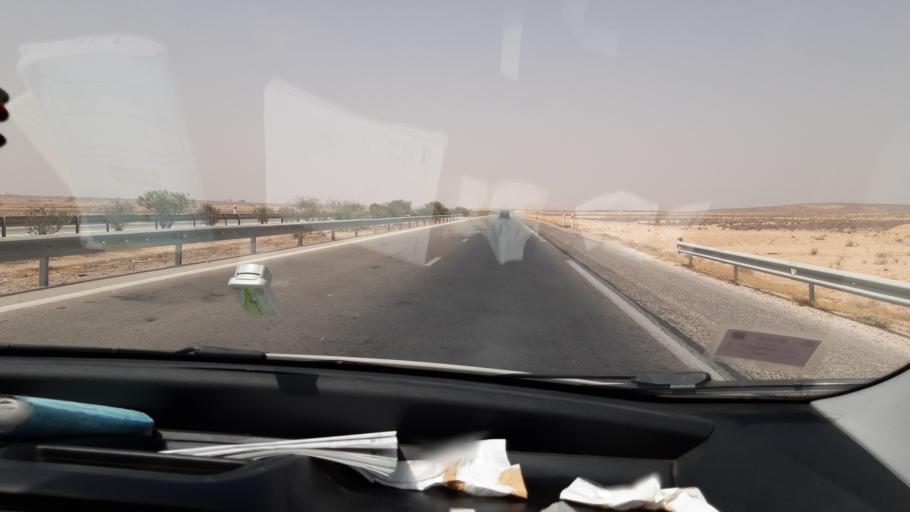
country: TN
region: Qabis
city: Gabes
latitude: 33.8983
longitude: 9.9819
